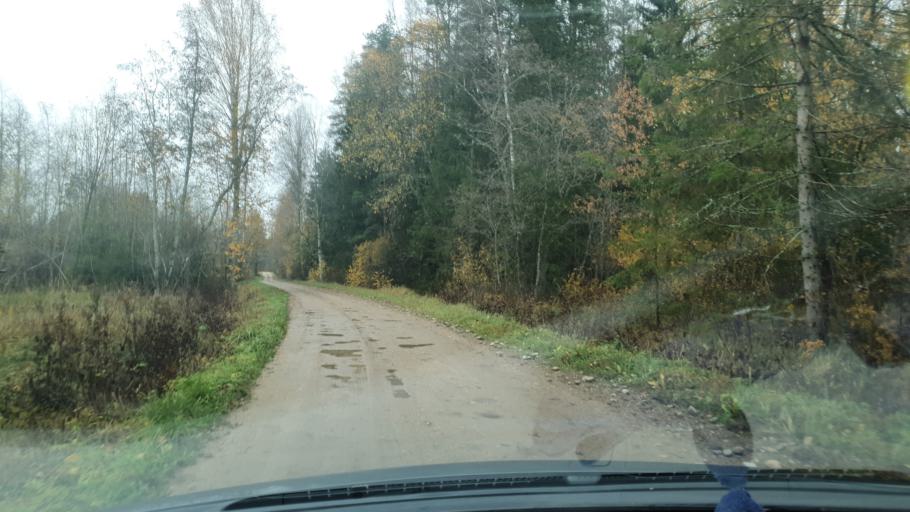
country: EE
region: Viljandimaa
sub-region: Karksi vald
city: Karksi-Nuia
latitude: 57.9891
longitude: 25.6405
